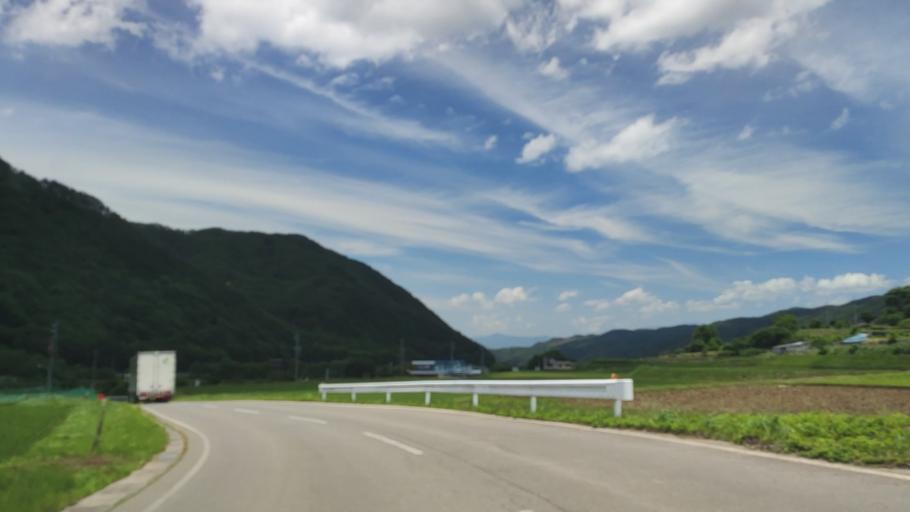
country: JP
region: Nagano
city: Kamimaruko
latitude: 36.2423
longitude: 138.2589
